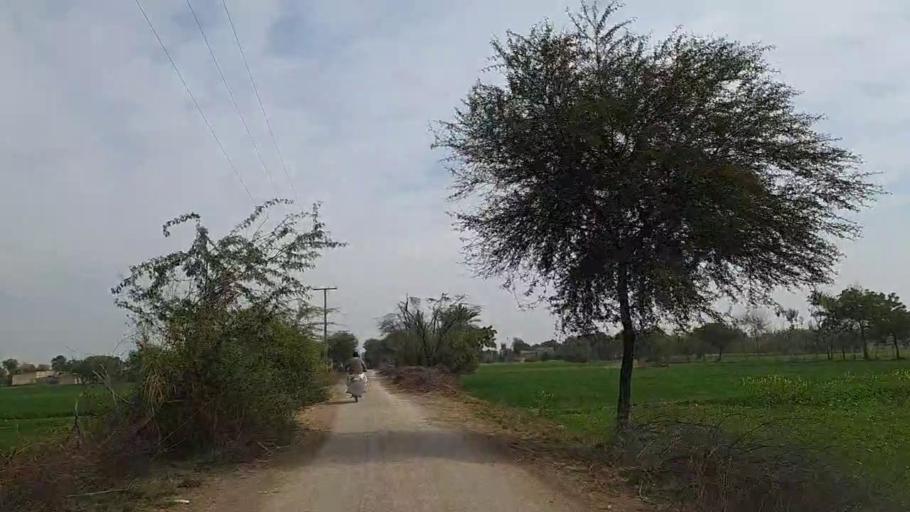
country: PK
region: Sindh
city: Nawabshah
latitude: 26.3853
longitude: 68.4393
